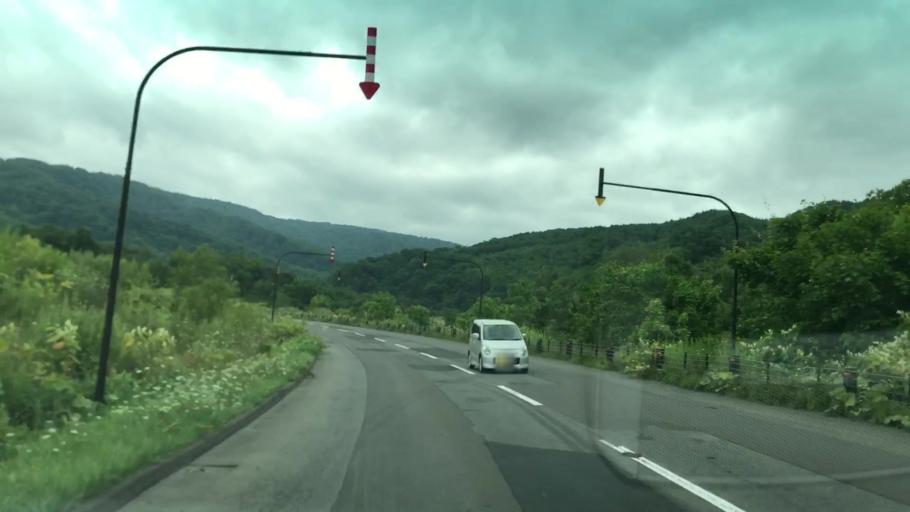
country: JP
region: Hokkaido
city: Yoichi
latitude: 43.0110
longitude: 140.8693
